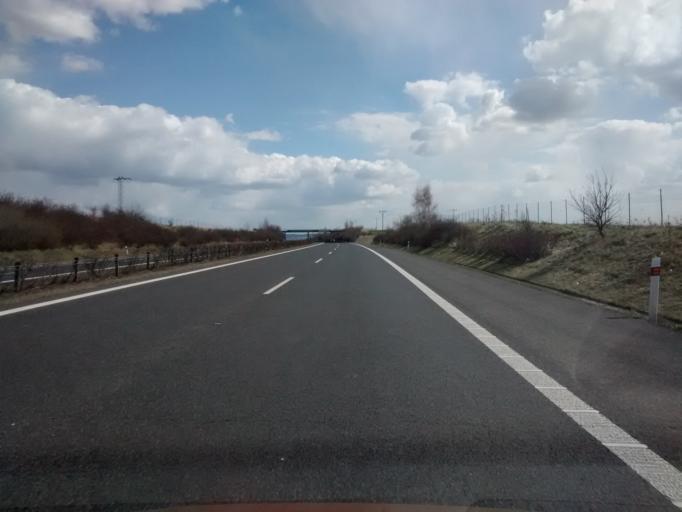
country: CZ
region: Central Bohemia
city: Nelahozeves
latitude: 50.3321
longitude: 14.2887
